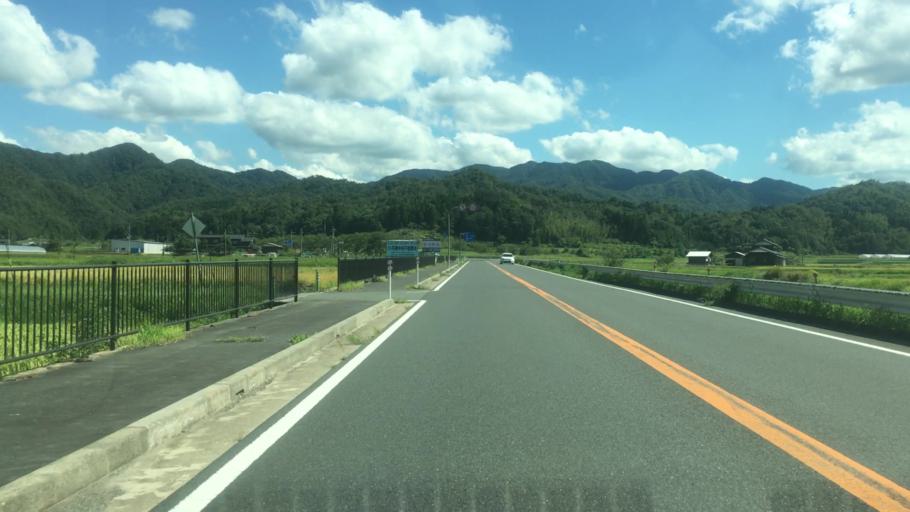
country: JP
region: Hyogo
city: Toyooka
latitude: 35.5770
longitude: 134.9742
